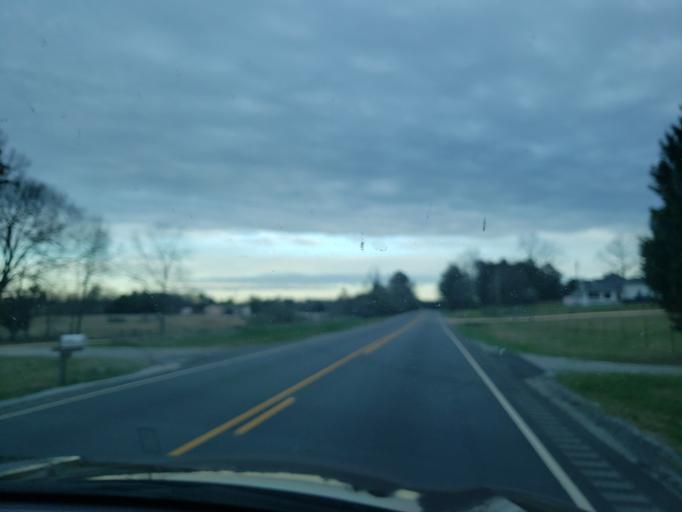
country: US
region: Alabama
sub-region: Randolph County
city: Roanoke
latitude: 33.0675
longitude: -85.3336
